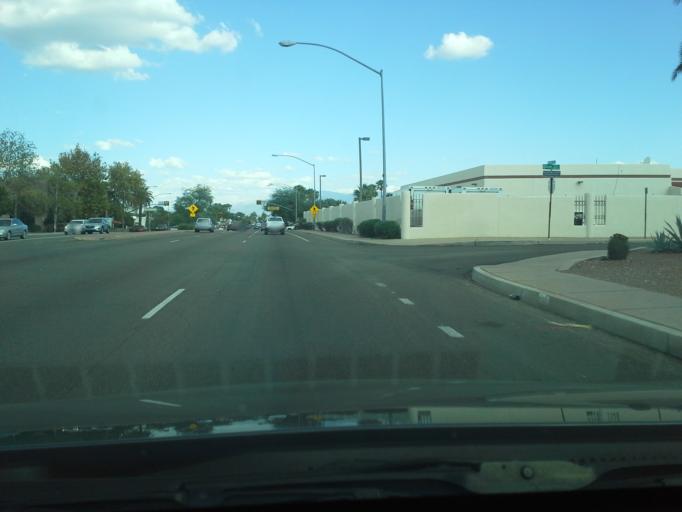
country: US
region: Arizona
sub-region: Pima County
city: Tucson
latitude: 32.2360
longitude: -110.9414
